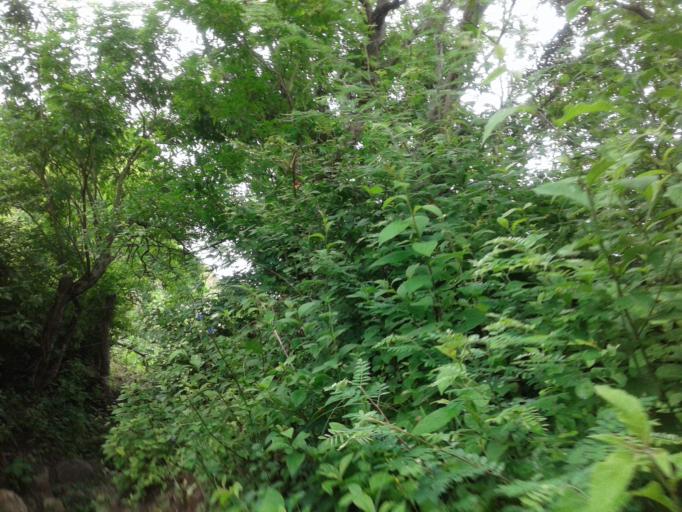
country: NI
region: Leon
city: Santa Rosa del Penon
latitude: 12.9102
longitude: -86.2252
